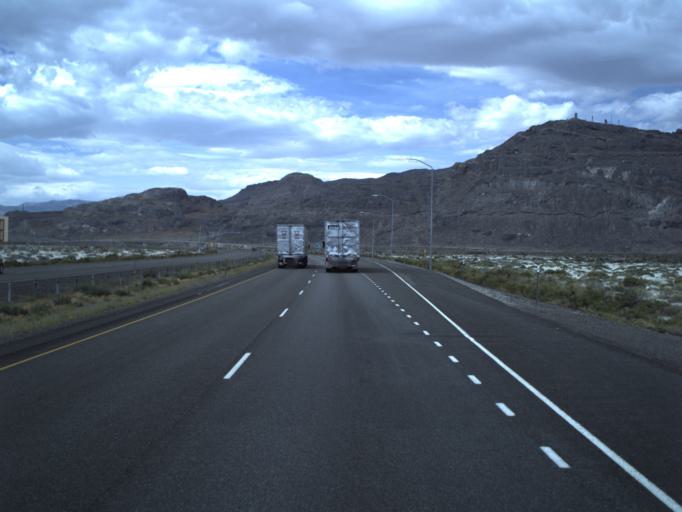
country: US
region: Utah
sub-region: Tooele County
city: Wendover
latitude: 40.7469
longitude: -114.0001
